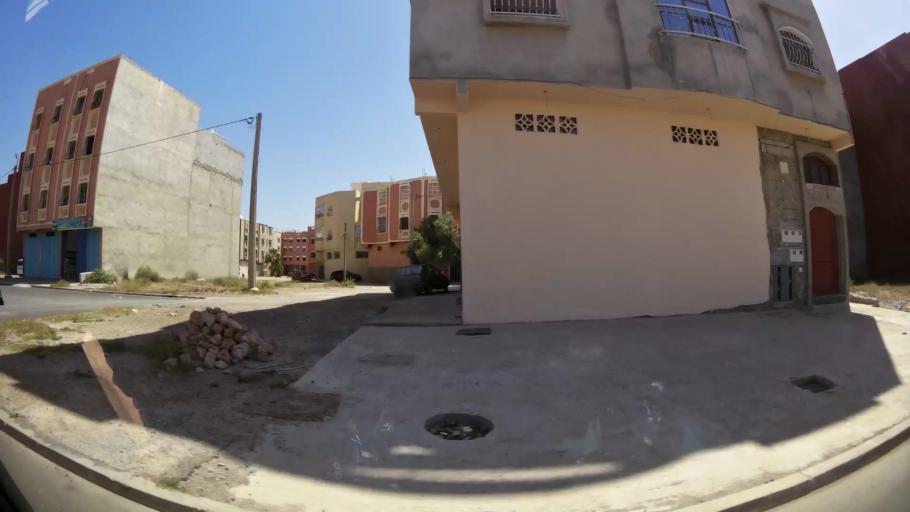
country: MA
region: Souss-Massa-Draa
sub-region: Inezgane-Ait Mellou
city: Inezgane
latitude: 30.3261
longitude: -9.5001
